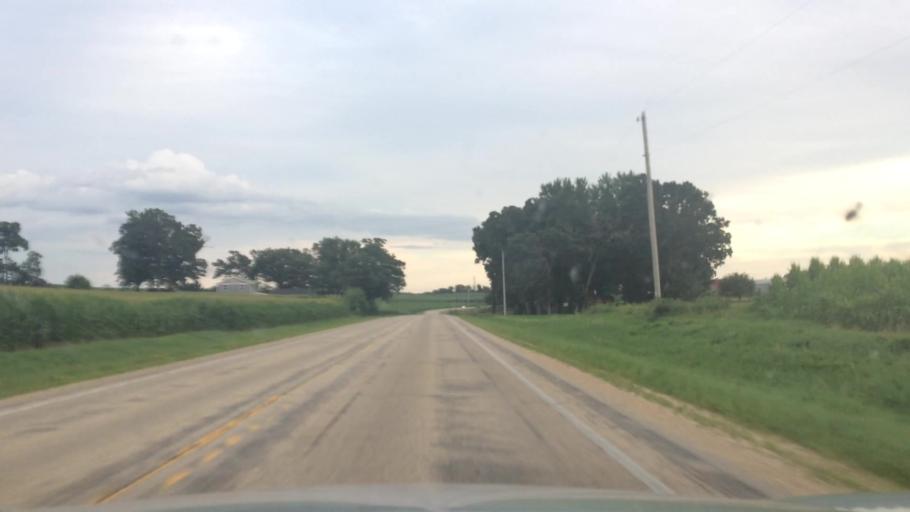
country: US
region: Wisconsin
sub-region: Dane County
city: Waunakee
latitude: 43.2180
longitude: -89.5461
